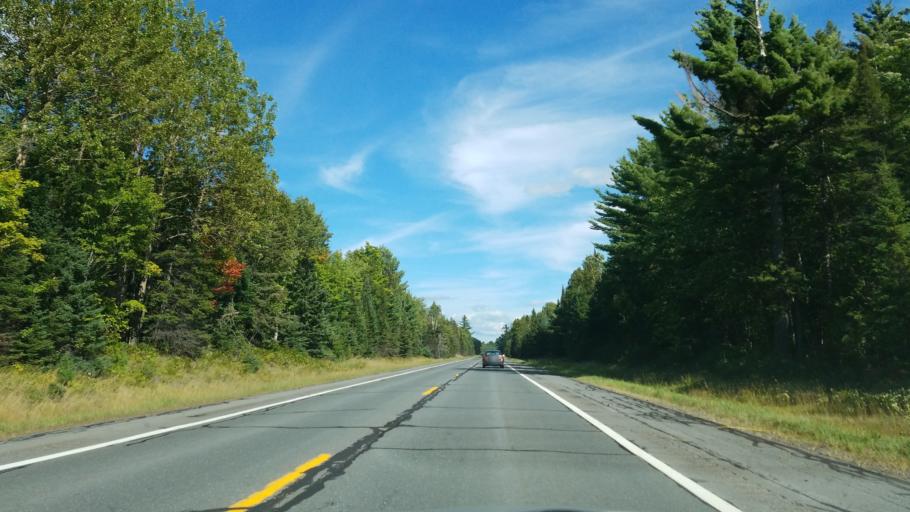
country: US
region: Michigan
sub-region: Baraga County
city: L'Anse
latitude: 46.5789
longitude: -88.3913
